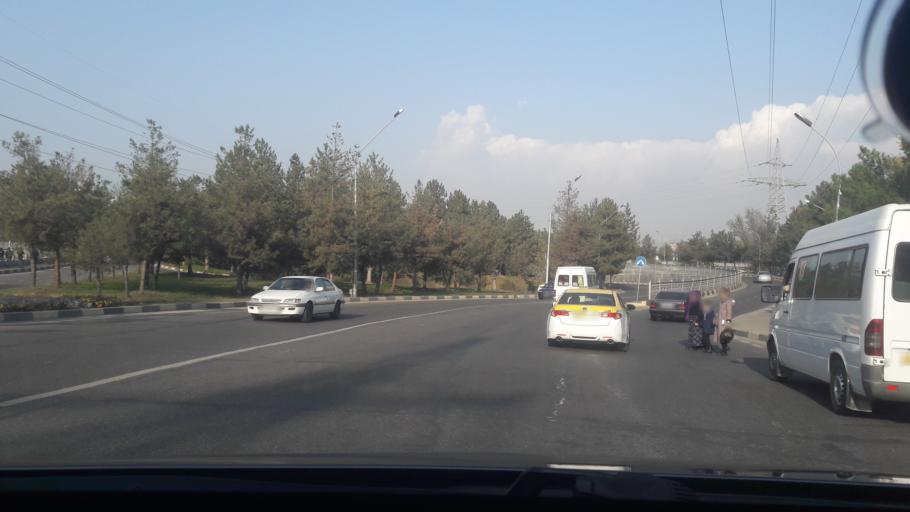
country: TJ
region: Dushanbe
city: Dushanbe
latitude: 38.5814
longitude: 68.7735
